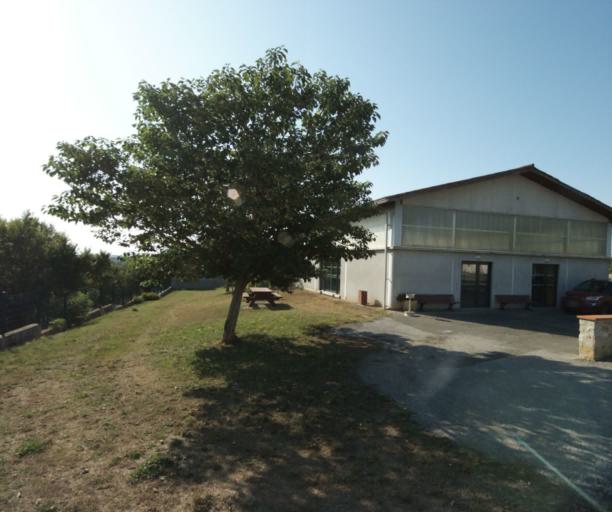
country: FR
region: Midi-Pyrenees
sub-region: Departement de la Haute-Garonne
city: Saint-Felix-Lauragais
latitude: 43.4414
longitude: 1.8218
